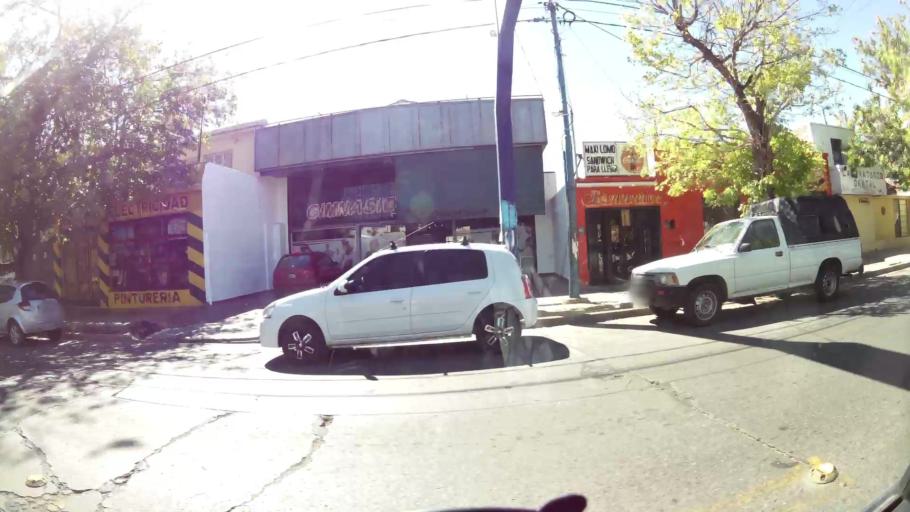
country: AR
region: Mendoza
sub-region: Departamento de Godoy Cruz
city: Godoy Cruz
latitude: -32.9102
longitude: -68.8602
